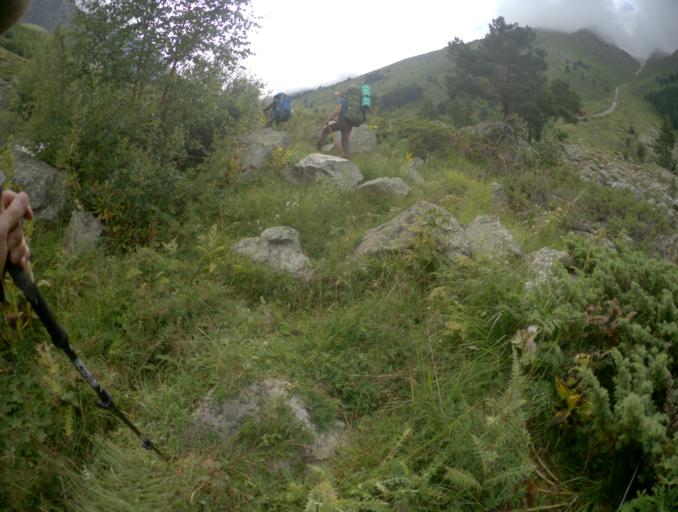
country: RU
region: Karachayevo-Cherkesiya
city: Uchkulan
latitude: 43.3401
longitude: 42.1381
